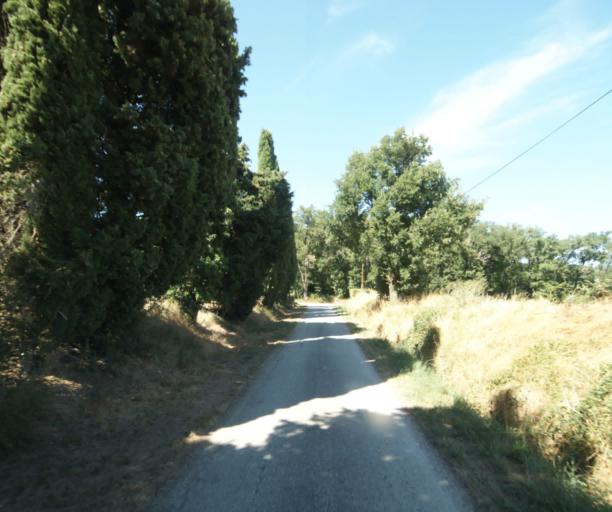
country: FR
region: Midi-Pyrenees
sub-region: Departement de la Haute-Garonne
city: Saint-Felix-Lauragais
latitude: 43.5104
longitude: 1.9146
